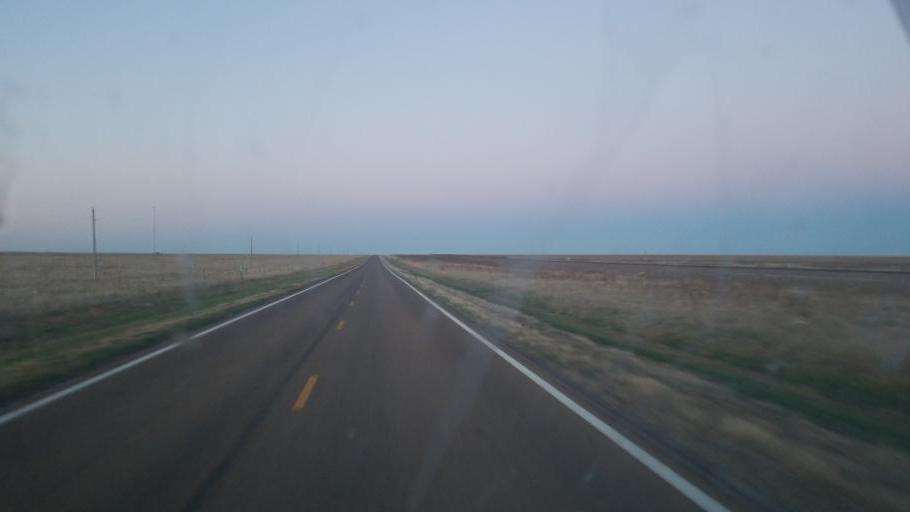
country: US
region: Kansas
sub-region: Wallace County
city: Sharon Springs
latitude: 38.9615
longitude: -101.4652
